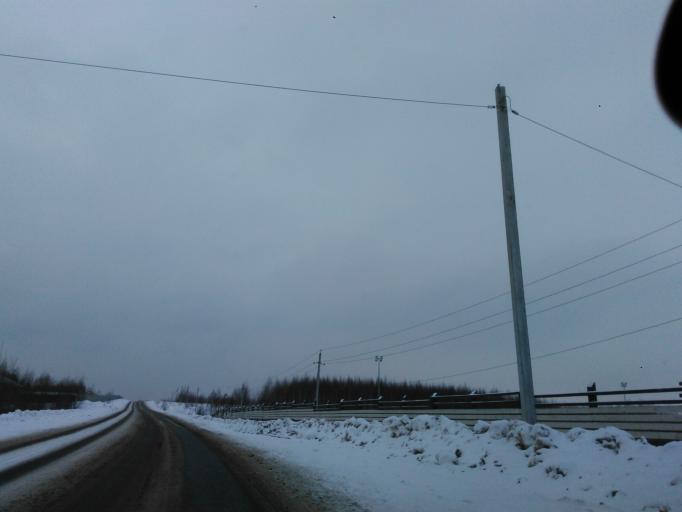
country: RU
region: Moskovskaya
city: Yakhroma
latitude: 56.2680
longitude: 37.4672
